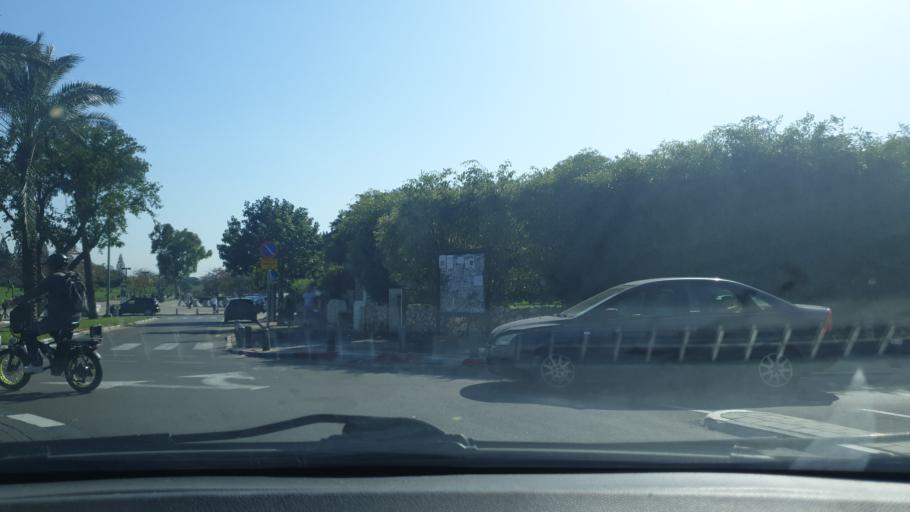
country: IL
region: Tel Aviv
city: Azor
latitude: 32.0443
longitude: 34.8043
